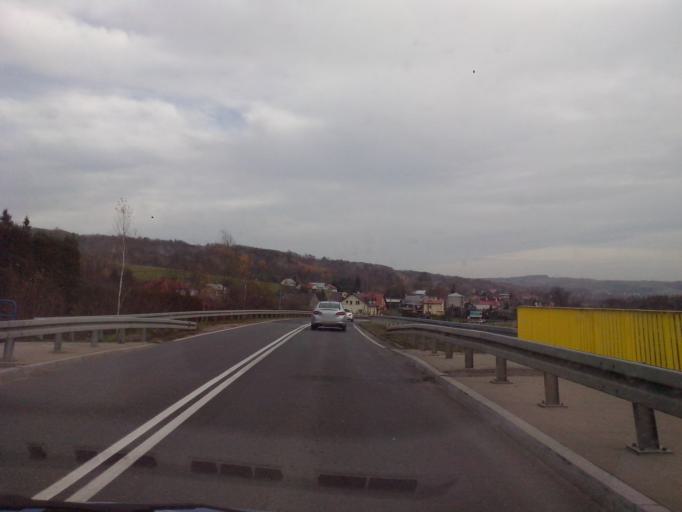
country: PL
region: Subcarpathian Voivodeship
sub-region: Powiat strzyzowski
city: Czudec
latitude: 49.9260
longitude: 21.8186
